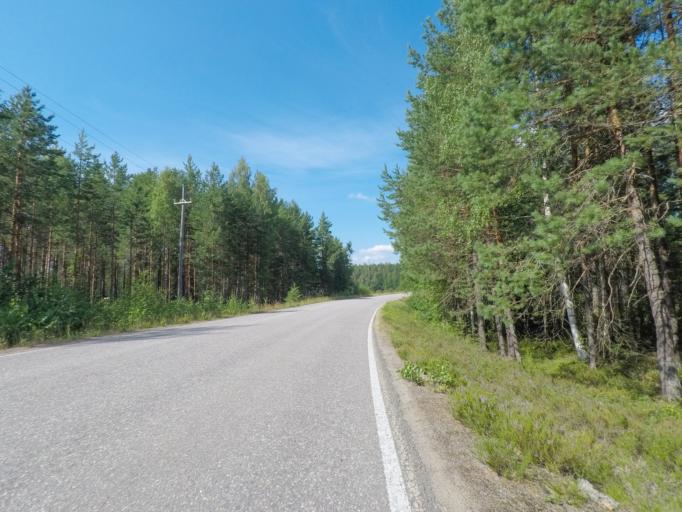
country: FI
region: Southern Savonia
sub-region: Mikkeli
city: Puumala
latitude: 61.4658
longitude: 28.1690
